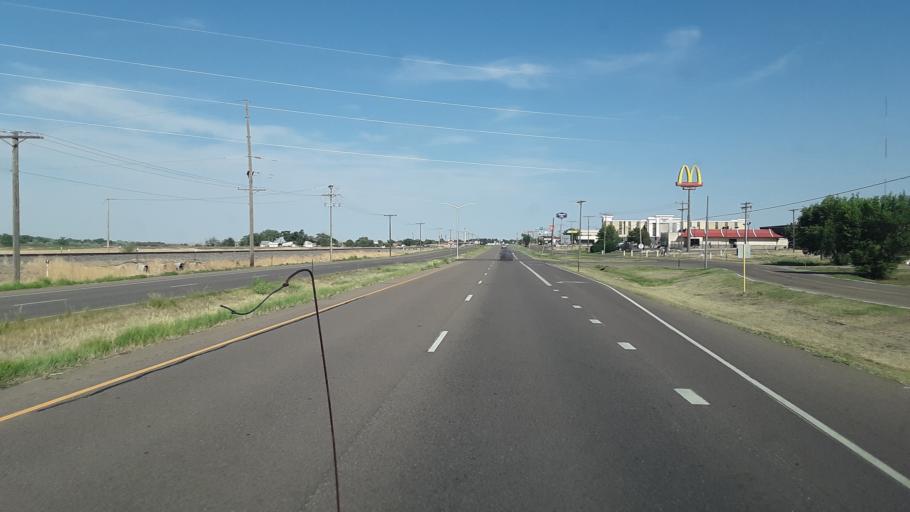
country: US
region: Colorado
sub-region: Otero County
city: La Junta
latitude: 37.9927
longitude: -103.5726
